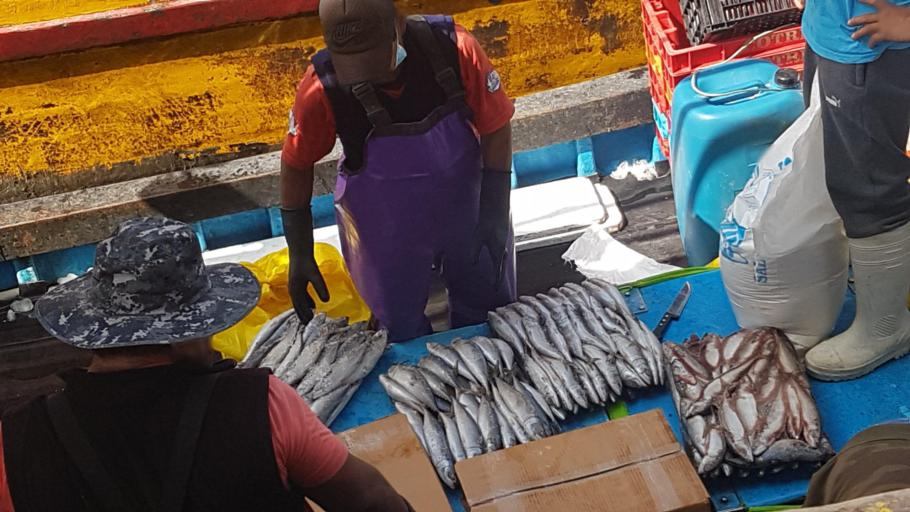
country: PE
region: Moquegua
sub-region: Provincia de Ilo
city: Ilo
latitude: -17.6452
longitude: -71.3450
